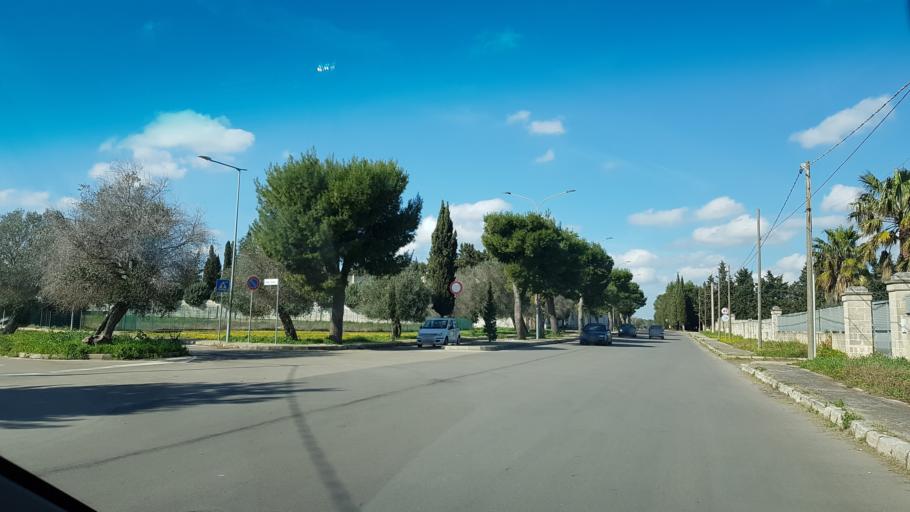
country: IT
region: Apulia
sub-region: Provincia di Lecce
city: Veglie
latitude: 40.3432
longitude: 17.9620
